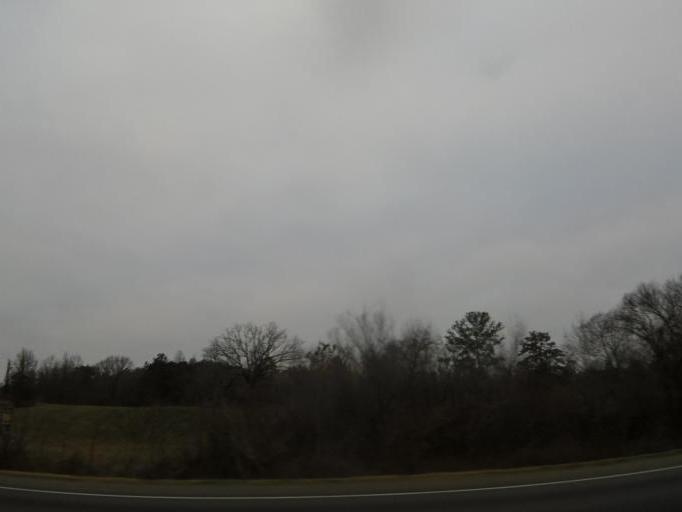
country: US
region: Alabama
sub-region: Jefferson County
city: Warrior
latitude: 33.8169
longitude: -86.8253
